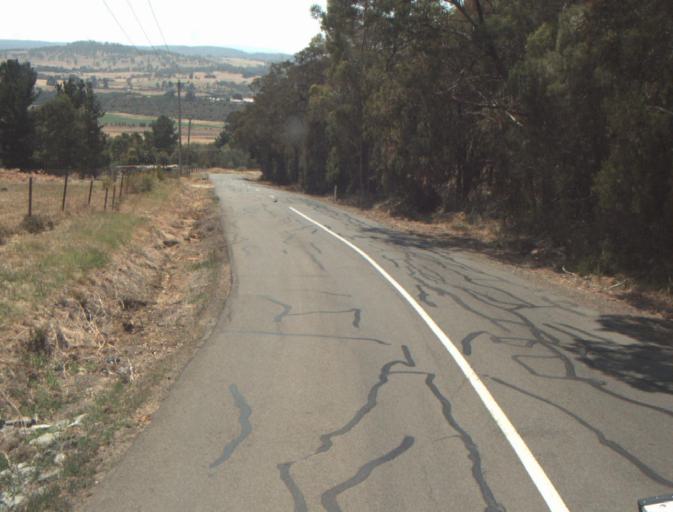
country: AU
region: Tasmania
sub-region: Launceston
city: Newstead
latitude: -41.4961
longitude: 147.2085
